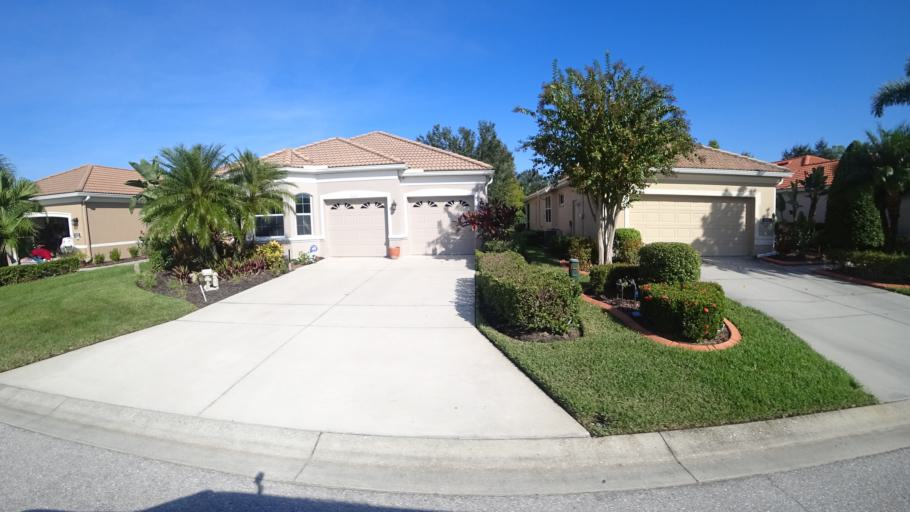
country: US
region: Florida
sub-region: Sarasota County
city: Desoto Lakes
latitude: 27.4292
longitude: -82.4612
